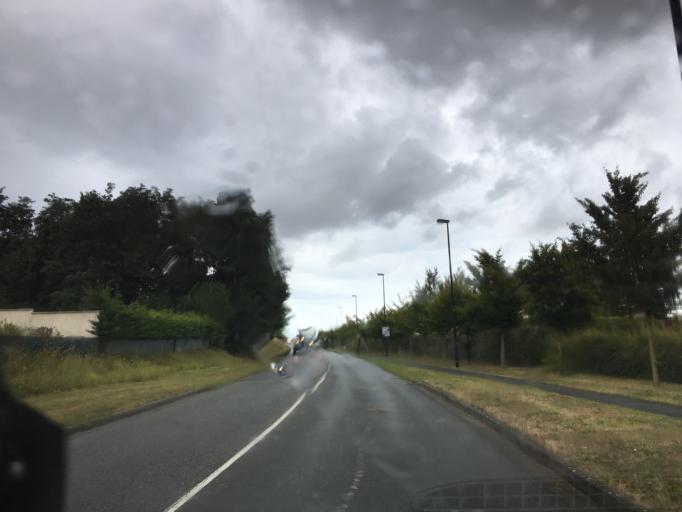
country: FR
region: Lower Normandy
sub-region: Departement du Calvados
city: Benouville
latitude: 49.2486
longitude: -0.2750
